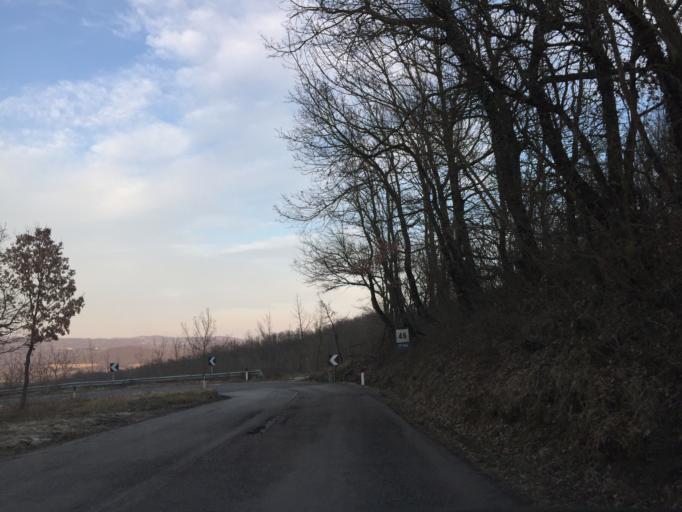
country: IT
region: Molise
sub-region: Provincia di Campobasso
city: Guardiaregia
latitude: 41.4489
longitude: 14.5551
